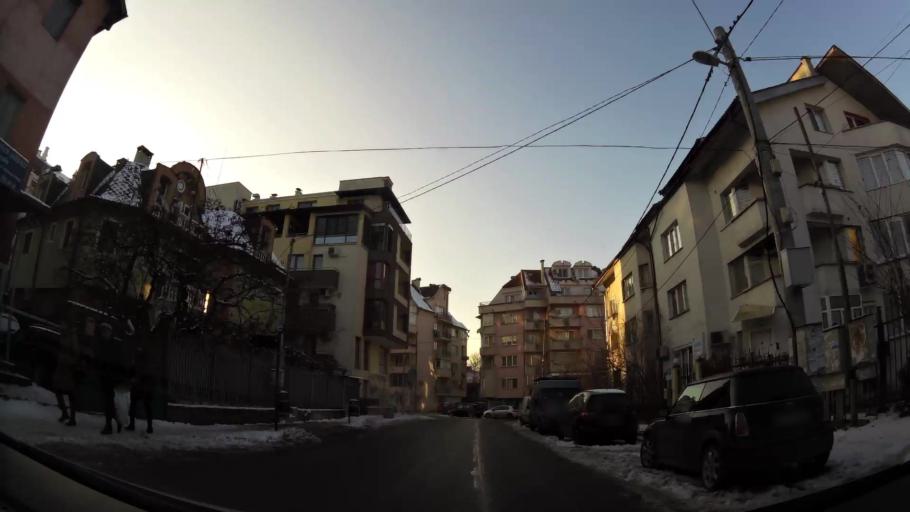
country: BG
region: Sofia-Capital
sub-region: Stolichna Obshtina
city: Sofia
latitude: 42.6900
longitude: 23.3591
